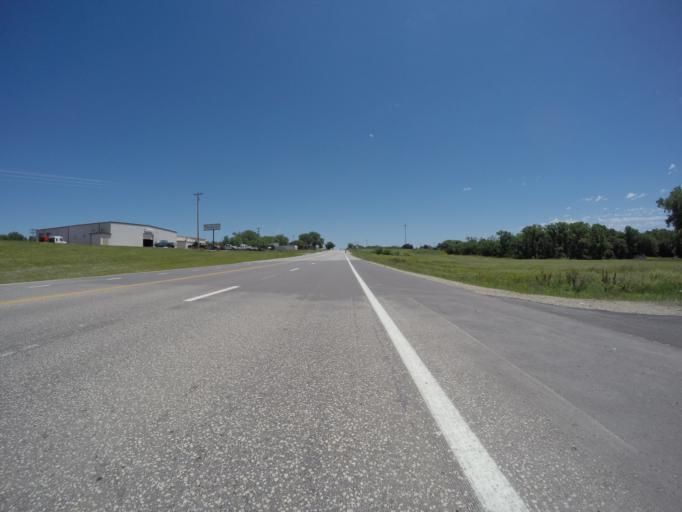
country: US
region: Kansas
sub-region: Republic County
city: Belleville
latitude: 39.8125
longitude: -97.6397
